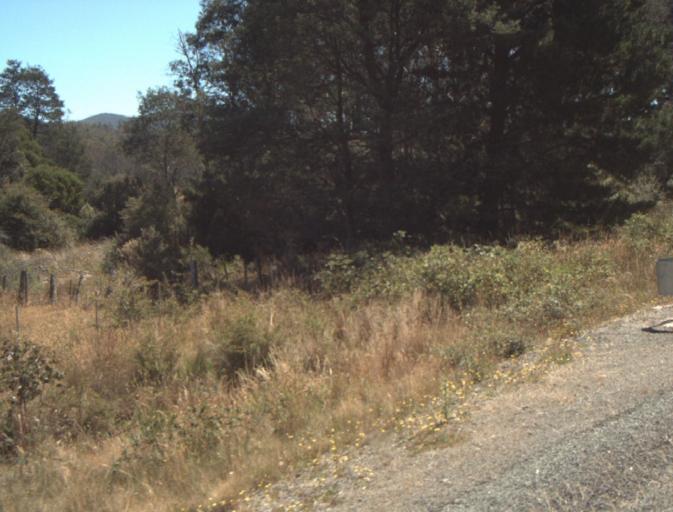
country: AU
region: Tasmania
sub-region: Launceston
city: Newstead
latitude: -41.3700
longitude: 147.3219
